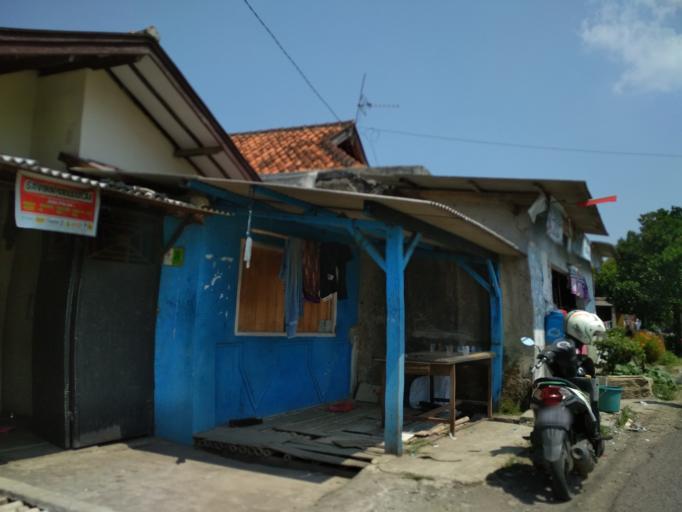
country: ID
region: West Java
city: Ciampea
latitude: -6.5517
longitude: 106.7414
